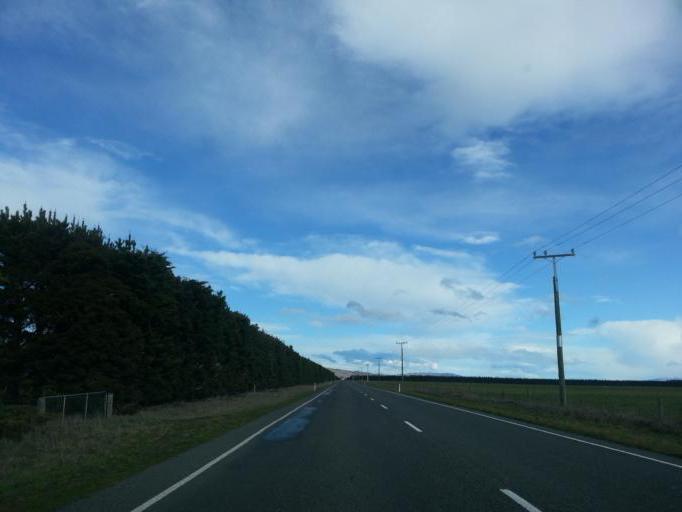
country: NZ
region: Canterbury
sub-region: Hurunui District
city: Amberley
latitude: -42.8061
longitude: 172.8224
